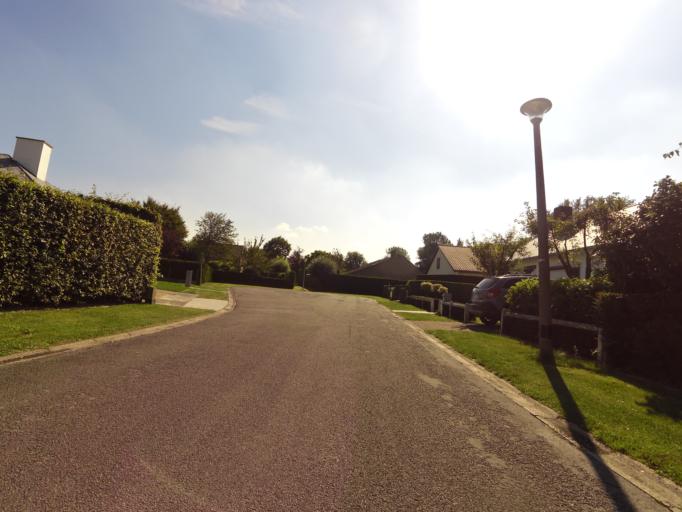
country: BE
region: Flanders
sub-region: Provincie West-Vlaanderen
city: Zuienkerke
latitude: 51.2063
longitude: 3.1568
